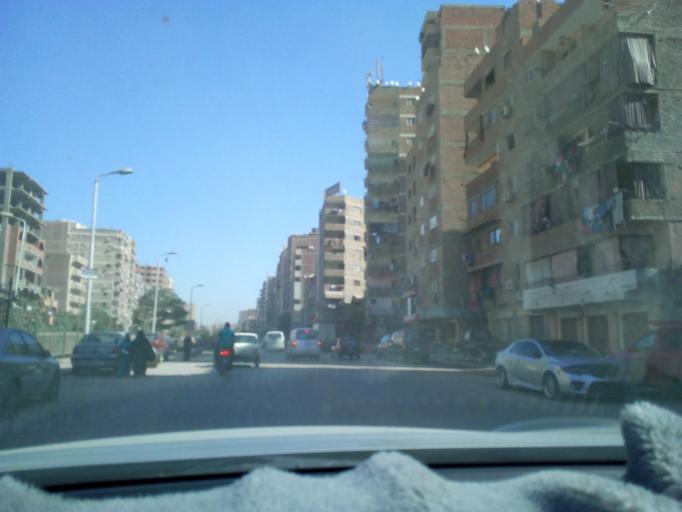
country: EG
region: Muhafazat al Qalyubiyah
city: Al Khankah
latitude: 30.1413
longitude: 31.3407
